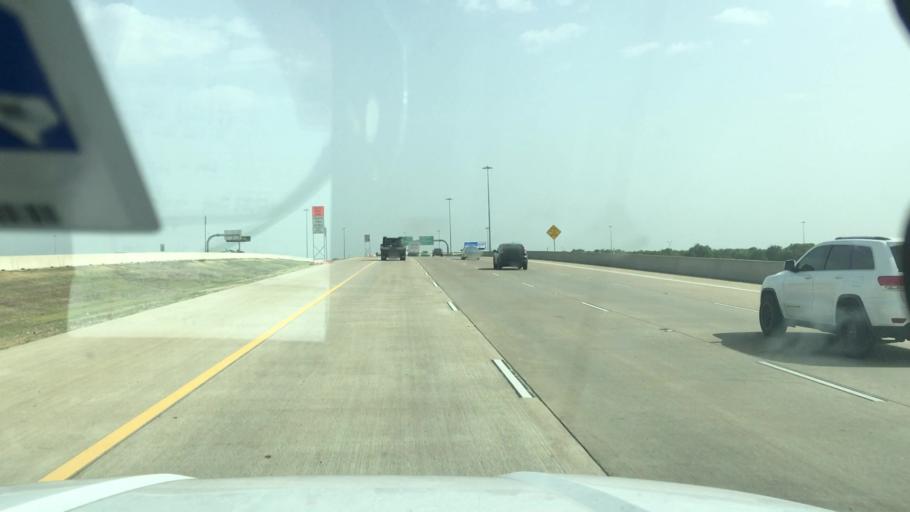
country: US
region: Texas
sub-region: Dallas County
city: Grand Prairie
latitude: 32.6843
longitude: -97.0243
